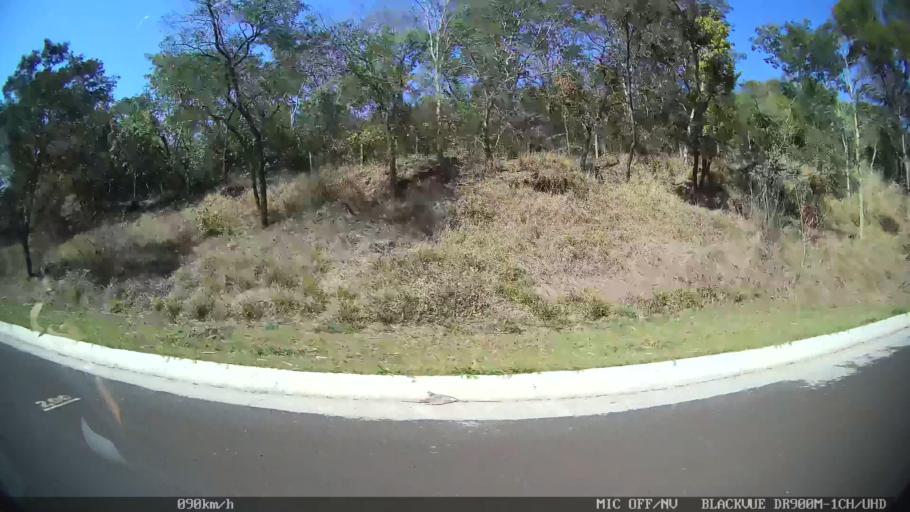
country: BR
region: Sao Paulo
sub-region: Batatais
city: Batatais
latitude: -20.7344
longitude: -47.5279
